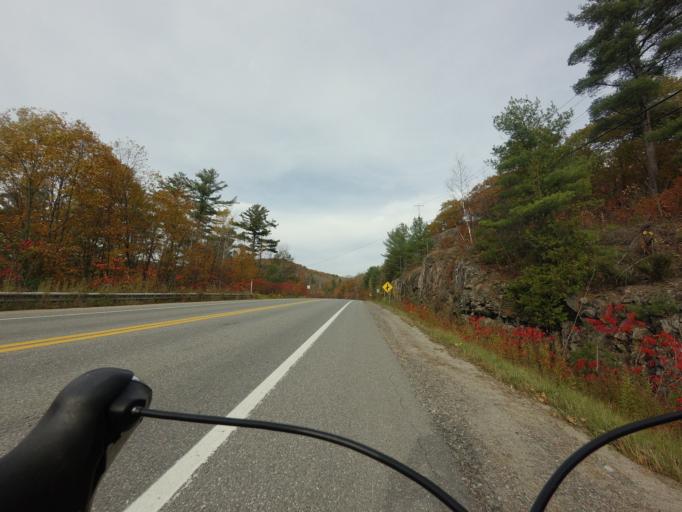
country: CA
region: Quebec
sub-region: Outaouais
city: Val-des-Monts
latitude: 45.6446
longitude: -75.6269
